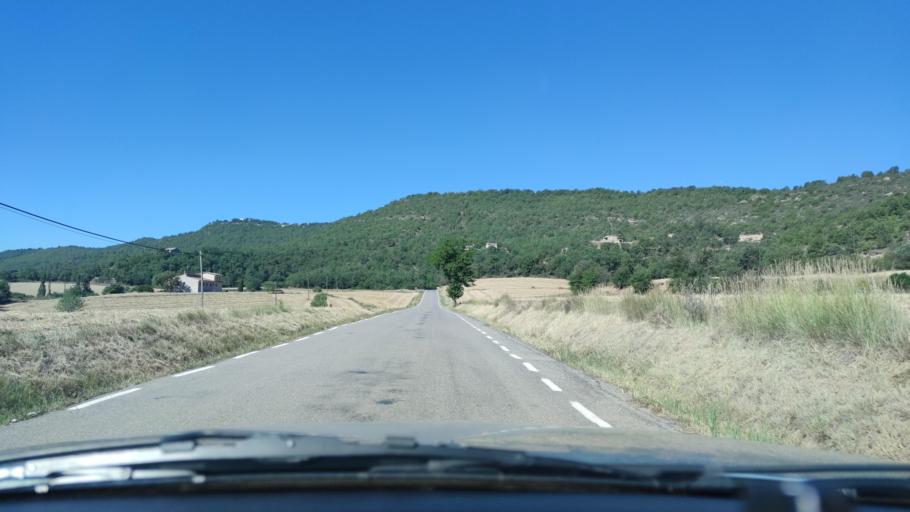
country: ES
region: Catalonia
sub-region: Provincia de Lleida
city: Solsona
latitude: 41.9766
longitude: 1.5026
